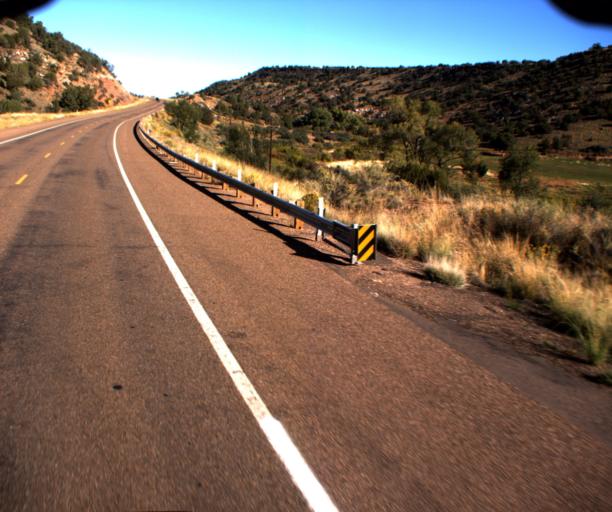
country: US
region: Arizona
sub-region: Navajo County
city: White Mountain Lake
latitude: 34.3901
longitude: -110.0640
